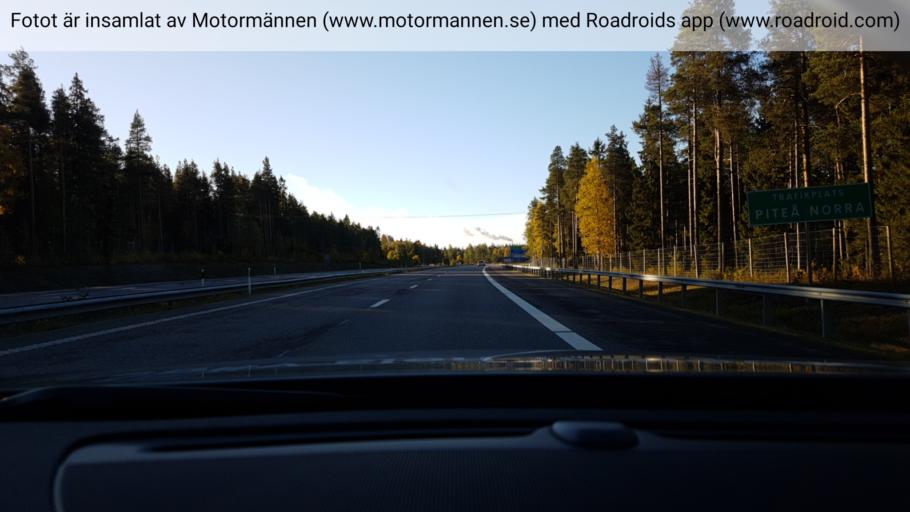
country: SE
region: Norrbotten
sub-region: Pitea Kommun
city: Pitea
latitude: 65.3382
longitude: 21.4402
